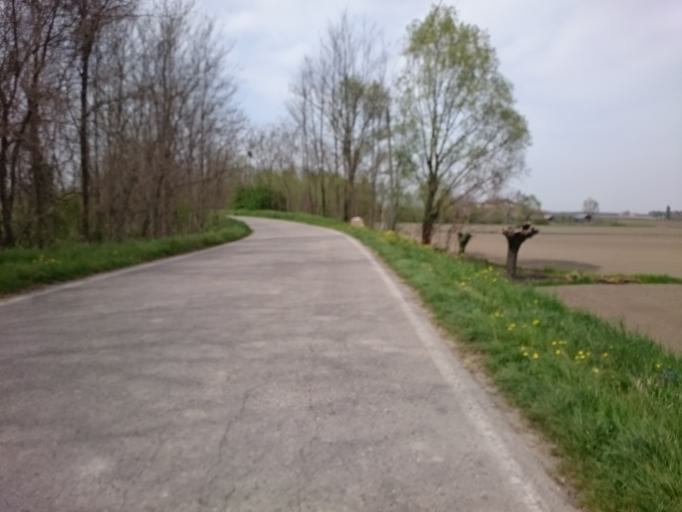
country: IT
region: Veneto
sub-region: Provincia di Padova
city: Anguillara Veneta
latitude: 45.1529
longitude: 11.8596
